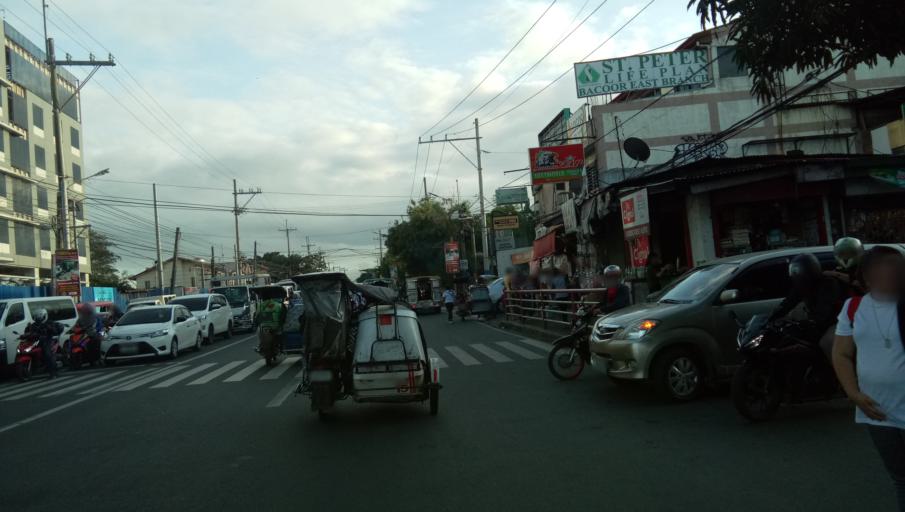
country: PH
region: Calabarzon
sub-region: Province of Cavite
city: Imus
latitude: 14.3831
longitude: 120.9783
